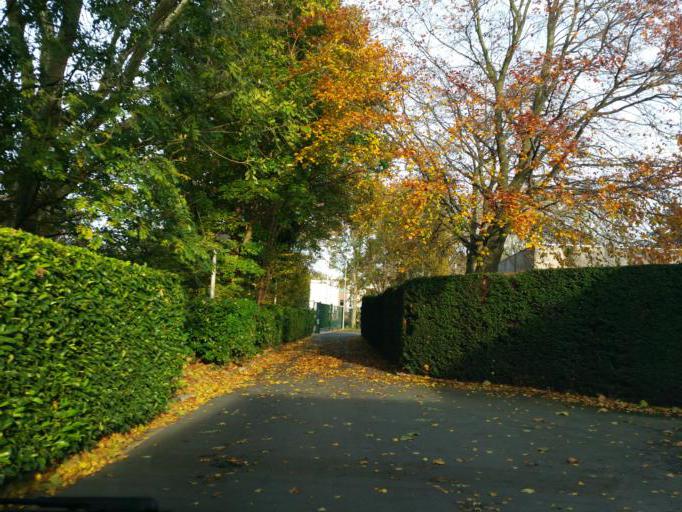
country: BE
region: Flanders
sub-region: Provincie Antwerpen
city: Hoboken
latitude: 51.1845
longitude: 4.3528
